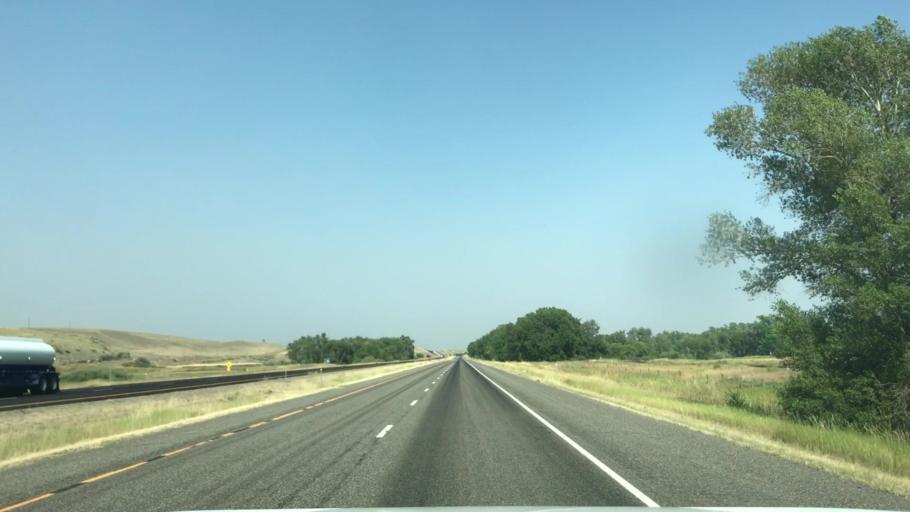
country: US
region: Montana
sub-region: Cascade County
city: Sun Prairie
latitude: 47.2328
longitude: -111.7505
